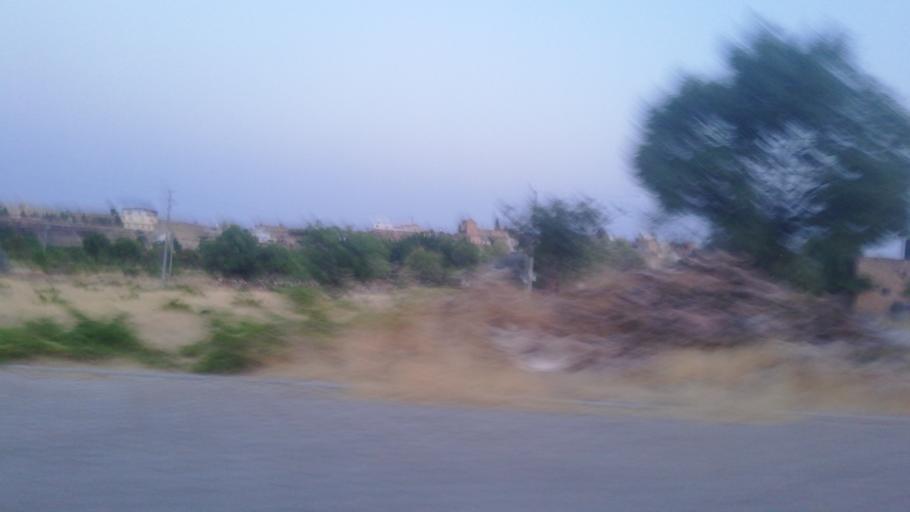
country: TR
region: Mardin
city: Kindirip
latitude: 37.4502
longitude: 41.2180
